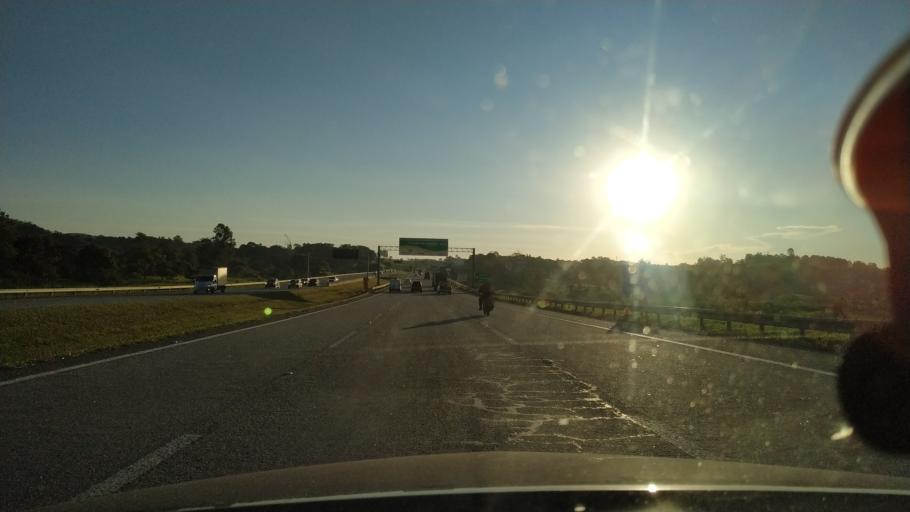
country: BR
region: Sao Paulo
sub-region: Sao Jose Dos Campos
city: Sao Jose dos Campos
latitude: -23.2704
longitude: -45.8296
